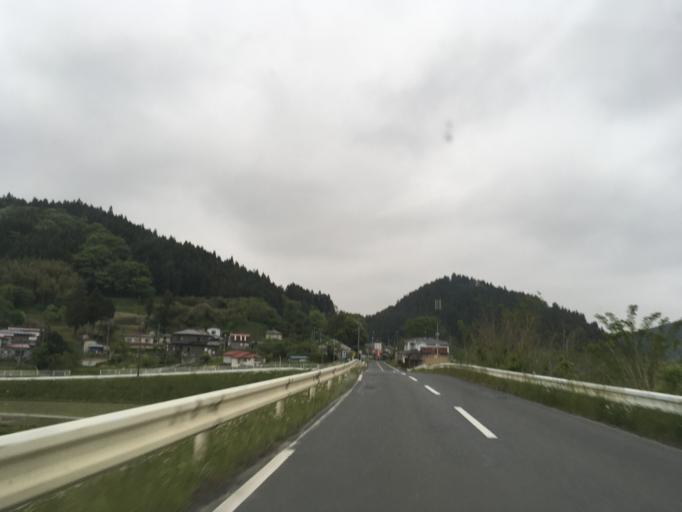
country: JP
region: Iwate
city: Ichinoseki
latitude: 38.7367
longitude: 141.3081
